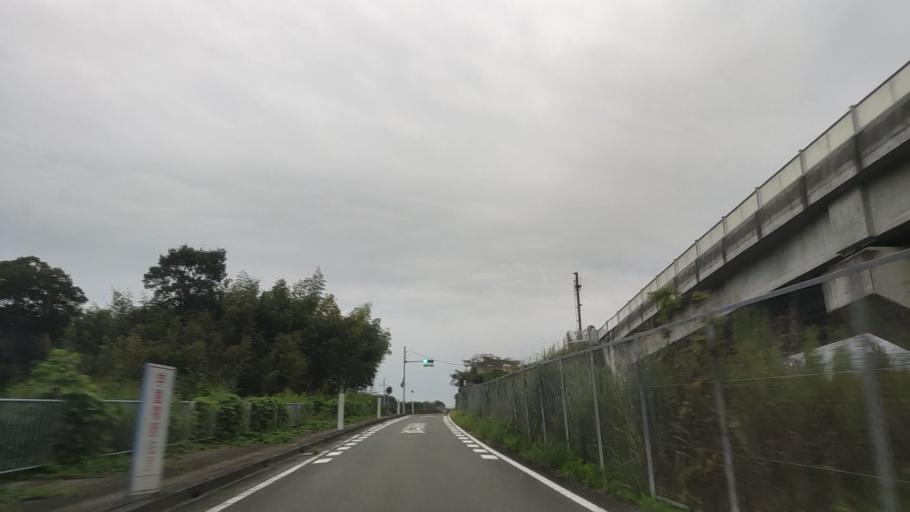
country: JP
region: Wakayama
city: Hashimoto
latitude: 34.3268
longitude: 135.6118
